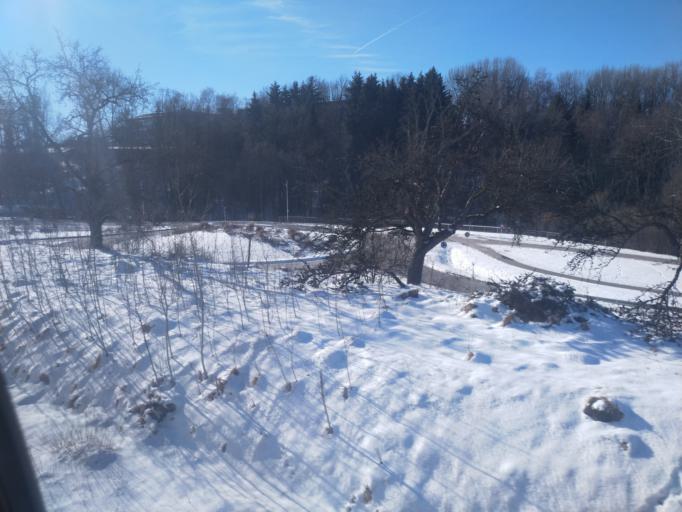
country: DE
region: Baden-Wuerttemberg
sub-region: Freiburg Region
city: Aldingen
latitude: 48.0991
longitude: 8.7094
